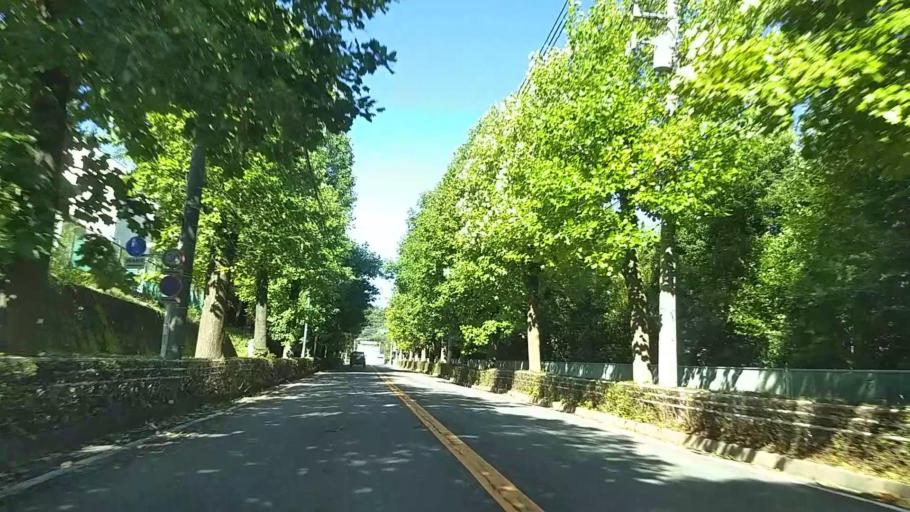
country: JP
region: Tokyo
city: Chofugaoka
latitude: 35.5900
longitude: 139.5479
